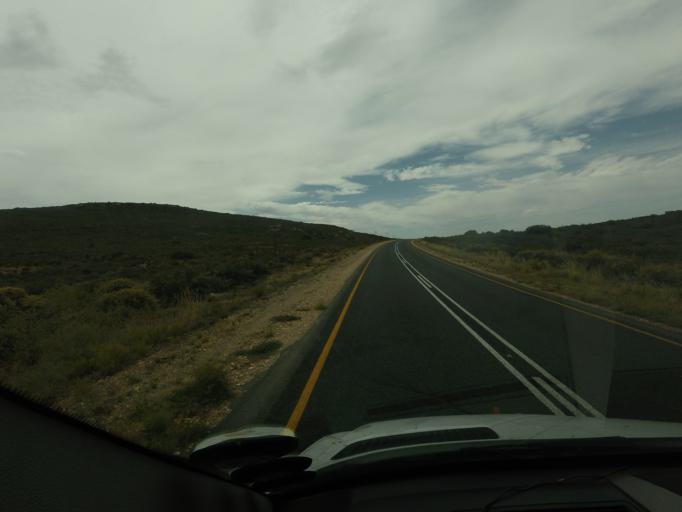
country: ZA
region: Western Cape
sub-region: Overberg District Municipality
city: Swellendam
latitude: -33.8643
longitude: 20.7667
